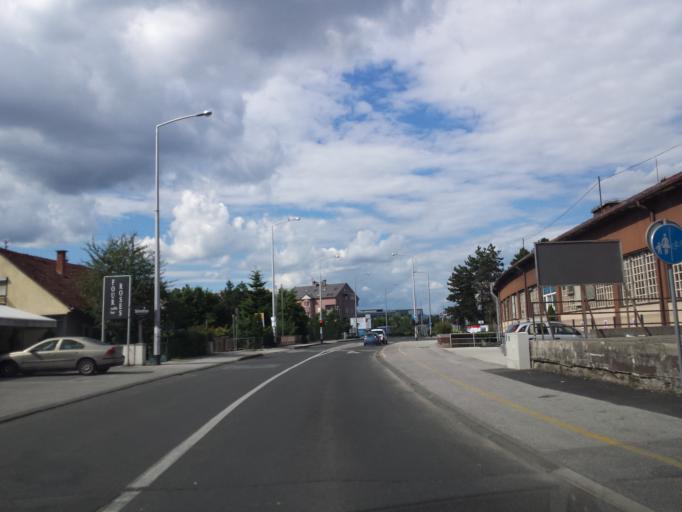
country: HR
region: Grad Zagreb
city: Novi Zagreb
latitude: 45.7704
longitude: 15.9502
